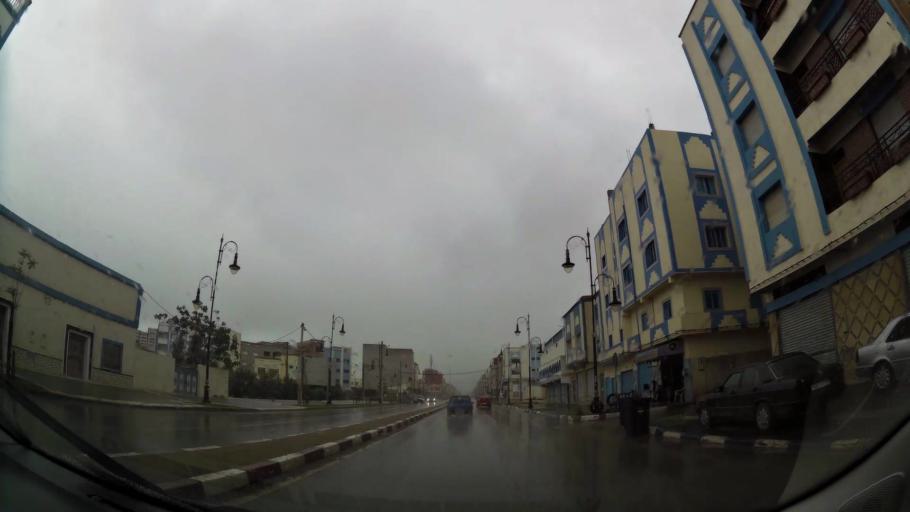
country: MA
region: Taza-Al Hoceima-Taounate
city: Imzourene
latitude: 35.1098
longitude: -3.8415
